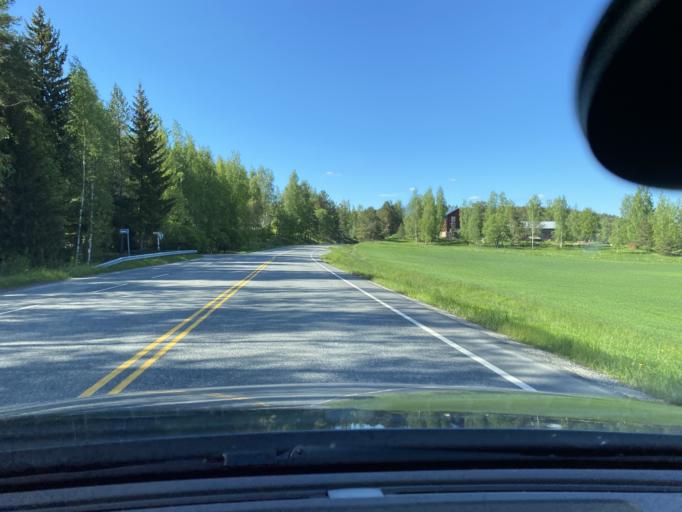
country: FI
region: Varsinais-Suomi
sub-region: Turku
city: Sauvo
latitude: 60.3764
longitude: 22.6687
